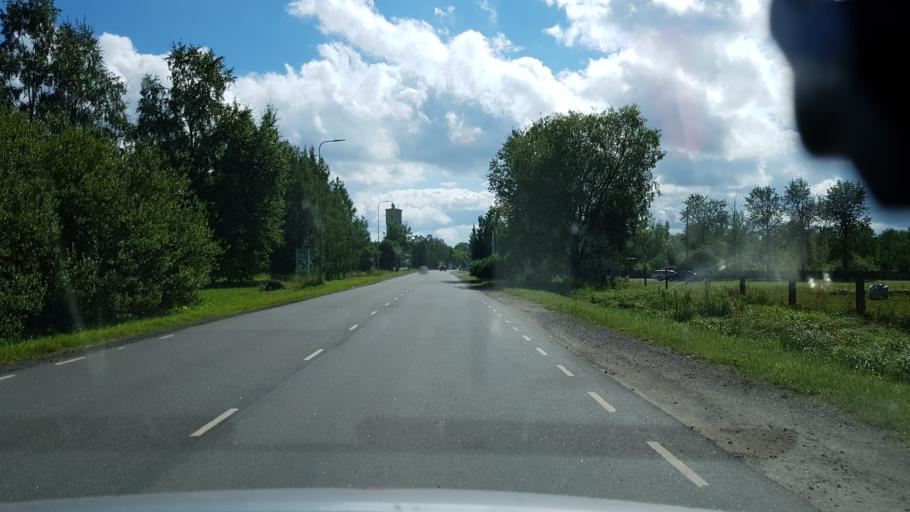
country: EE
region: Ida-Virumaa
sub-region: Kivioli linn
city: Kivioli
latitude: 59.3627
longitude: 26.9686
